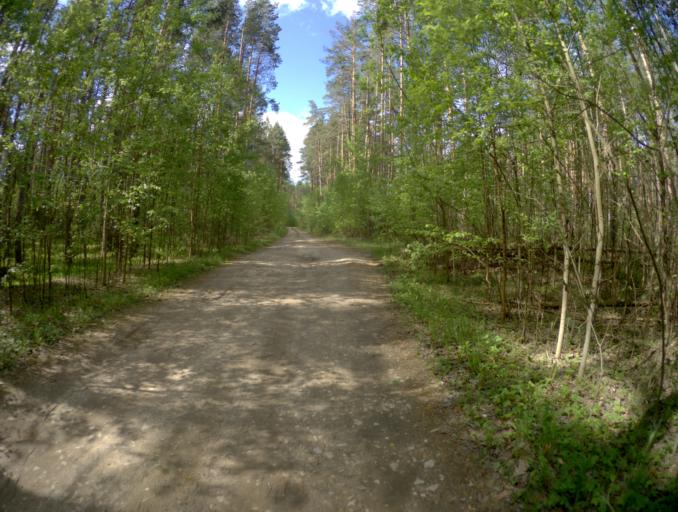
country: RU
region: Rjazan
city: Spas-Klepiki
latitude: 55.2416
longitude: 40.0634
